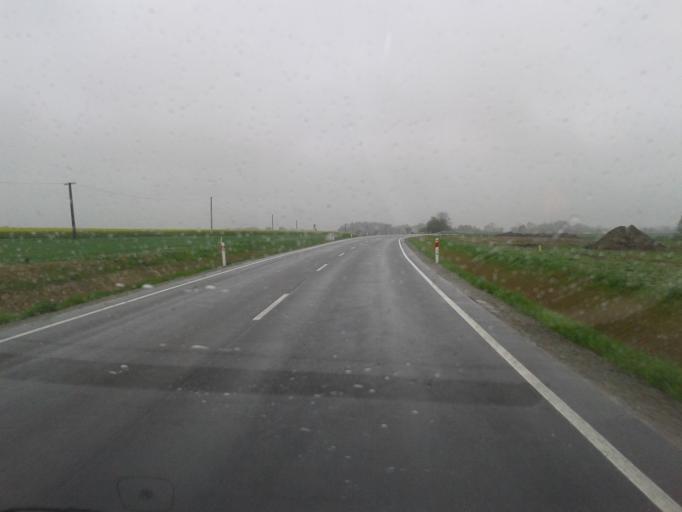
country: PL
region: Subcarpathian Voivodeship
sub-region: Powiat lubaczowski
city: Cieszanow
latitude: 50.2513
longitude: 23.1406
